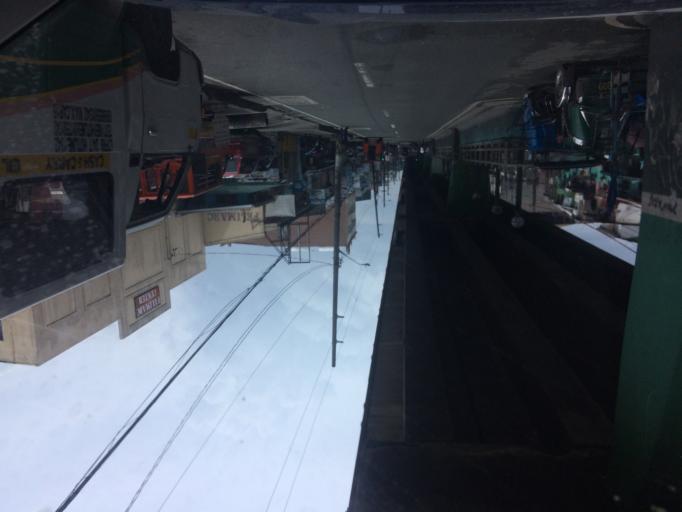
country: PH
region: Metro Manila
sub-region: Makati City
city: Makati City
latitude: 14.5521
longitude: 120.9976
